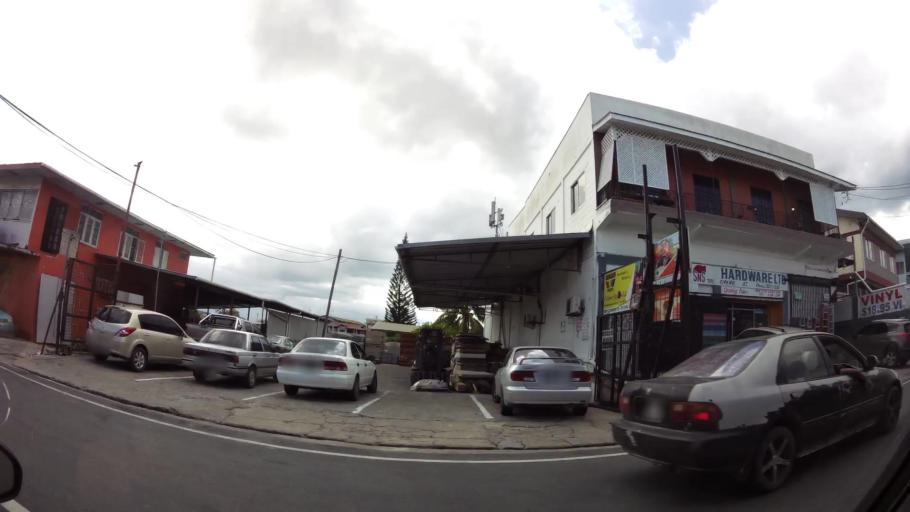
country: TT
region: City of San Fernando
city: San Fernando
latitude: 10.2704
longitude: -61.4599
